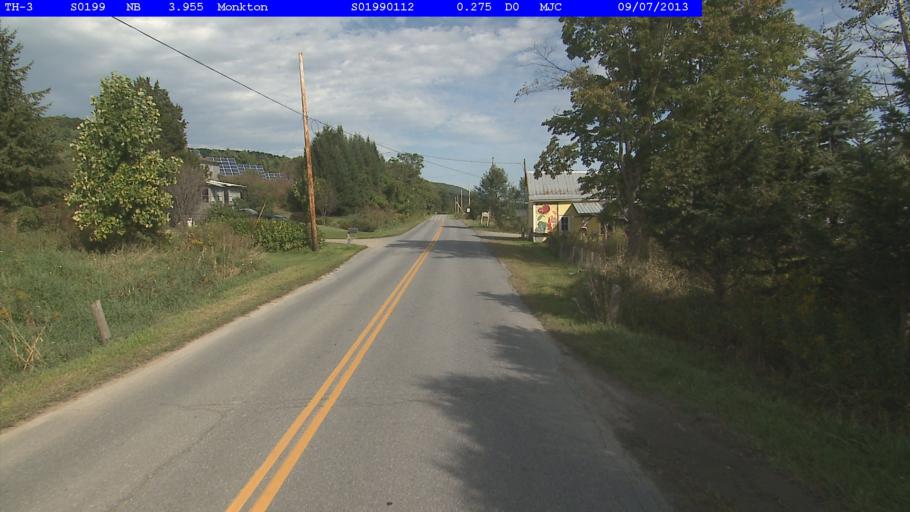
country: US
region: Vermont
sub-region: Addison County
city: Bristol
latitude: 44.1847
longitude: -73.1062
